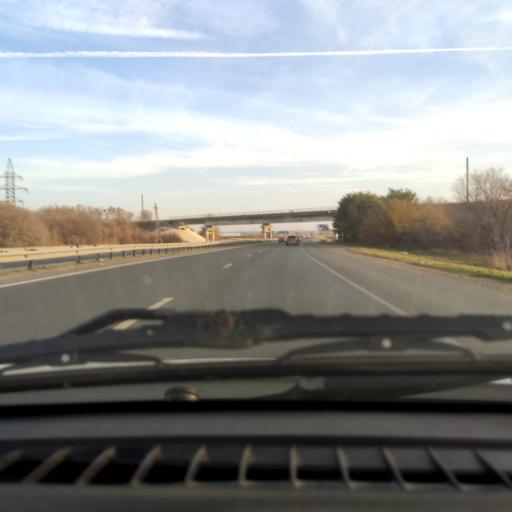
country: RU
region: Samara
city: Tol'yatti
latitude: 53.5643
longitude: 49.4960
